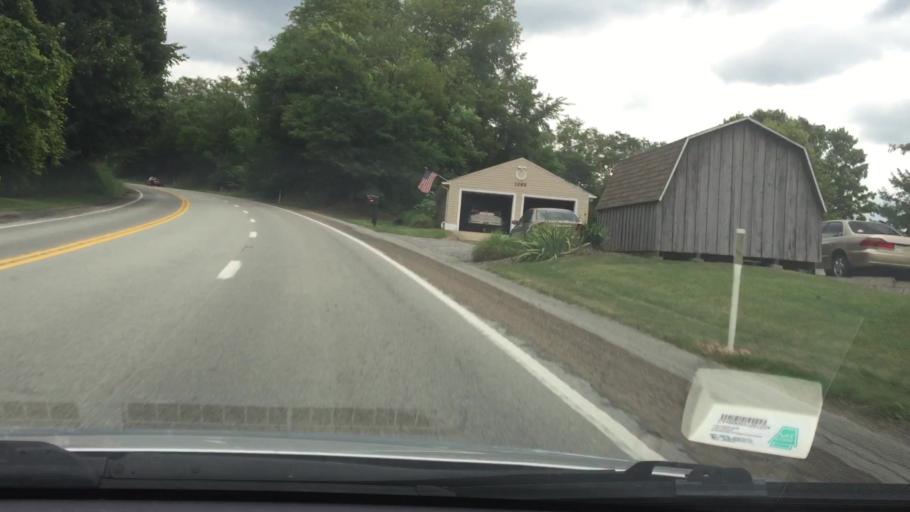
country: US
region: Pennsylvania
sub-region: Armstrong County
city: Freeport
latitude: 40.6815
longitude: -79.6934
